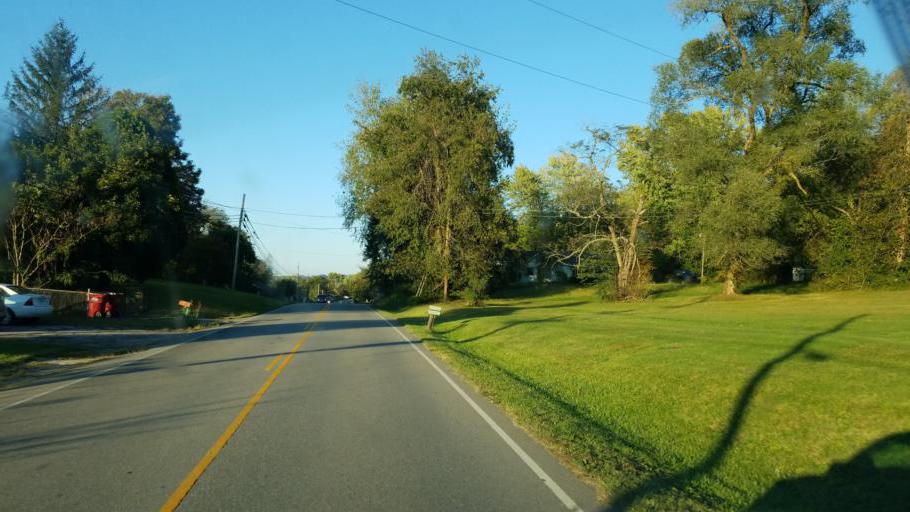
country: US
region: Ohio
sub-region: Scioto County
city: Portsmouth
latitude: 38.7137
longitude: -83.0239
